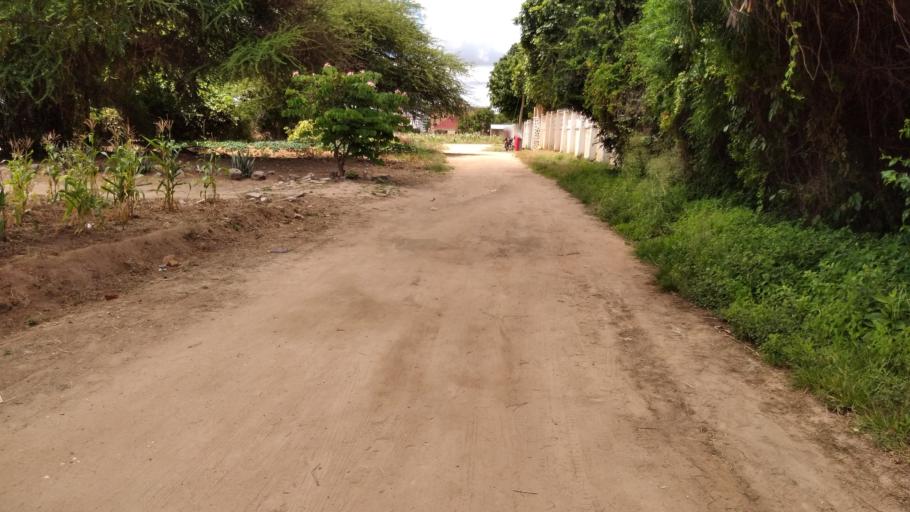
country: TZ
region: Dodoma
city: Dodoma
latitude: -6.1898
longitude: 35.7530
